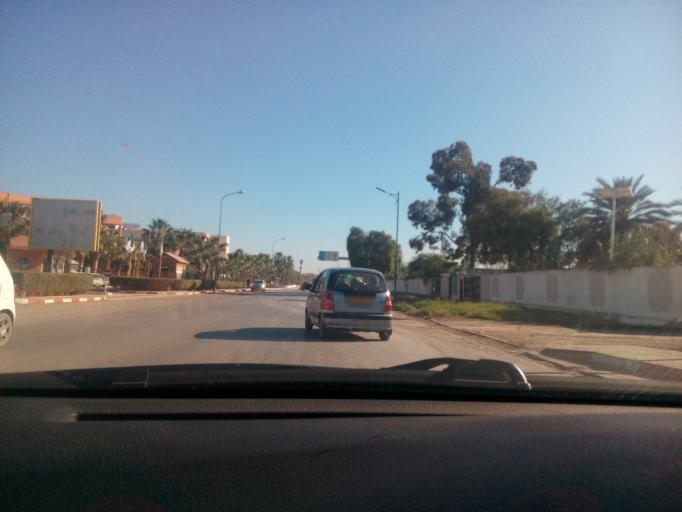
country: DZ
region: Oran
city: Es Senia
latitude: 35.6250
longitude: -0.5954
